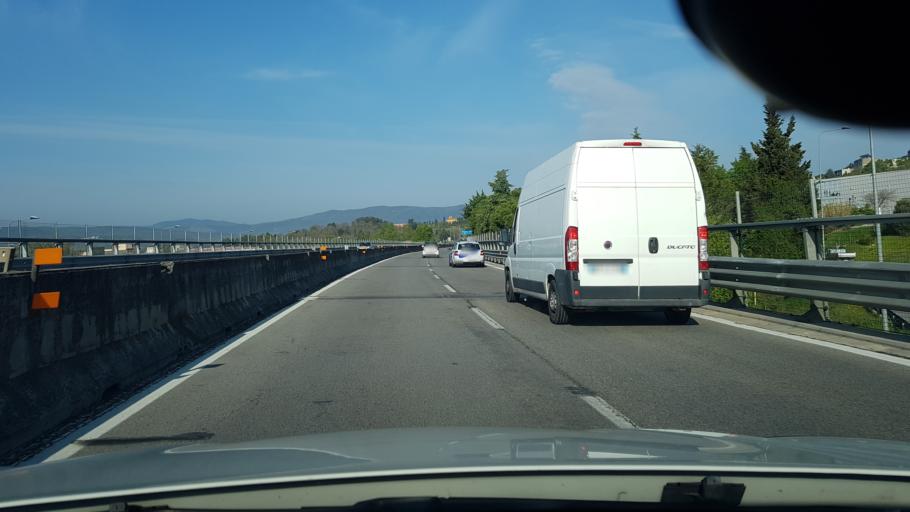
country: IT
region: Umbria
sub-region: Provincia di Perugia
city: Chiugiana-La Commenda
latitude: 43.1008
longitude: 12.3068
